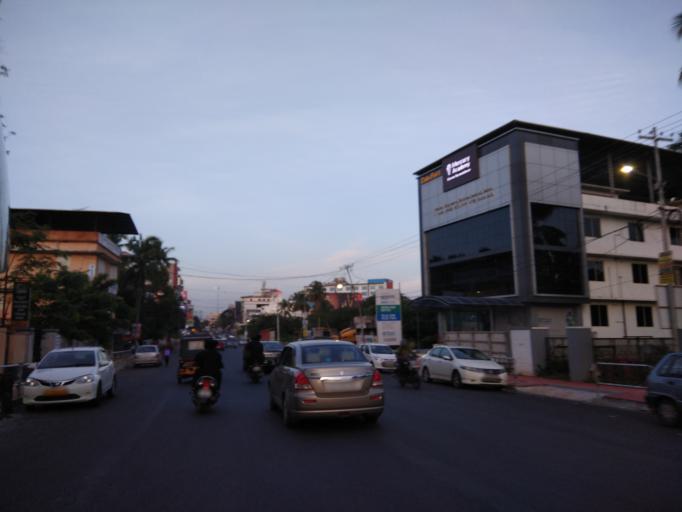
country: IN
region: Kerala
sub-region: Thrissur District
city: Trichur
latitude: 10.5219
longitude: 76.1989
